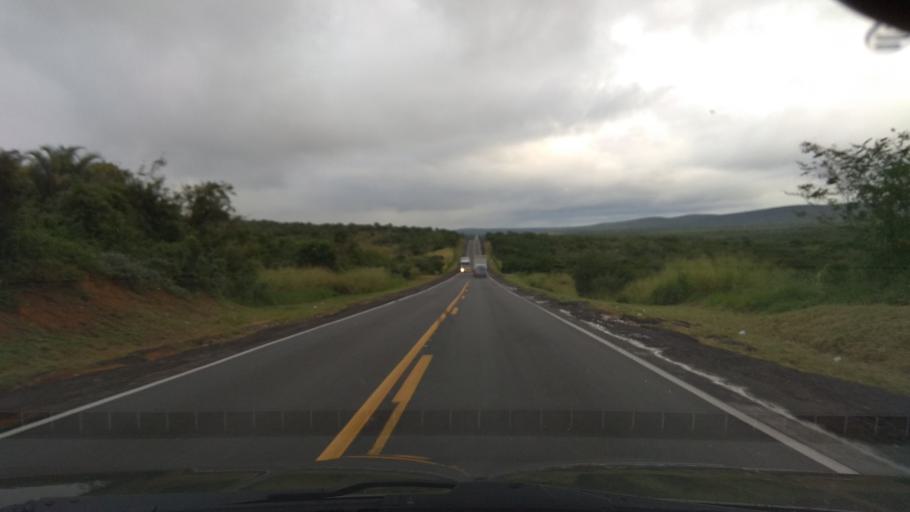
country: BR
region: Bahia
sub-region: Jaguaquara
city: Jaguaquara
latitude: -13.3850
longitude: -40.0213
